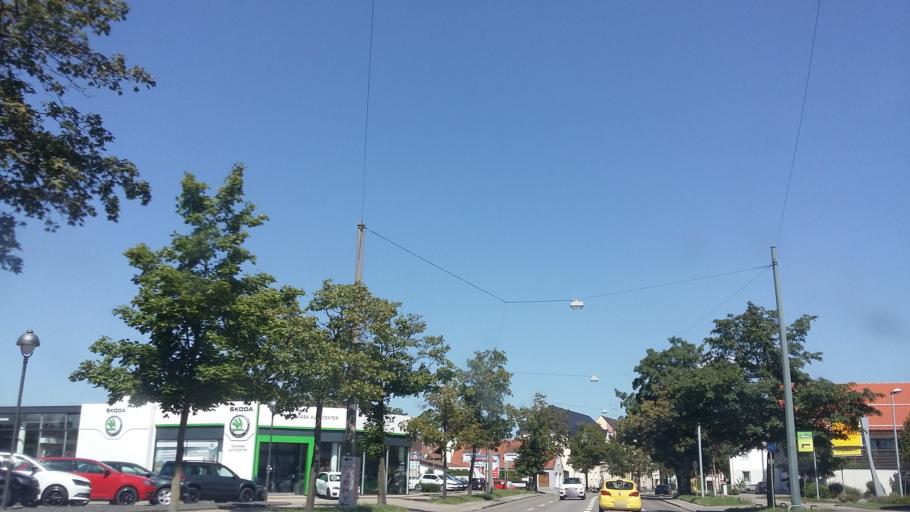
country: DE
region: Bavaria
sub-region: Swabia
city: Augsburg
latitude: 48.3879
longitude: 10.9160
